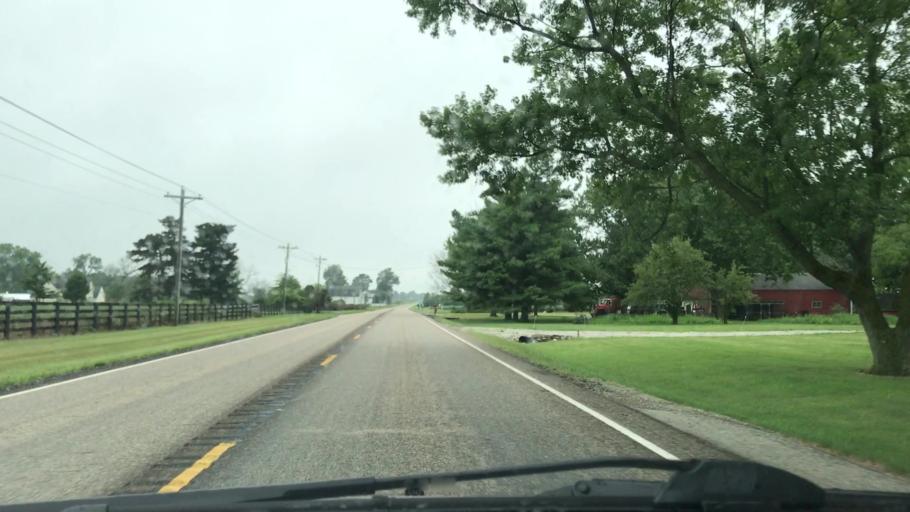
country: US
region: Indiana
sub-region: Boone County
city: Dale
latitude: 40.1274
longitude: -86.3522
